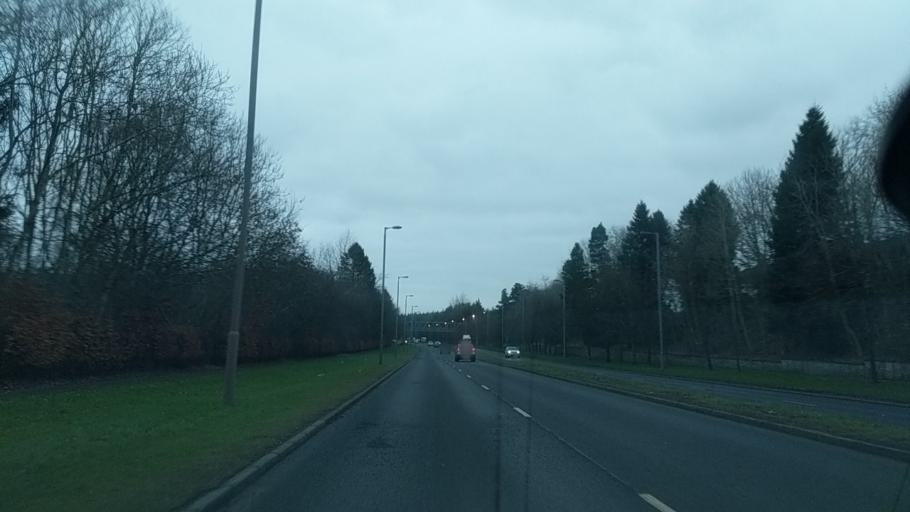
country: GB
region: Scotland
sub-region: South Lanarkshire
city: East Kilbride
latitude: 55.7702
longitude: -4.1647
